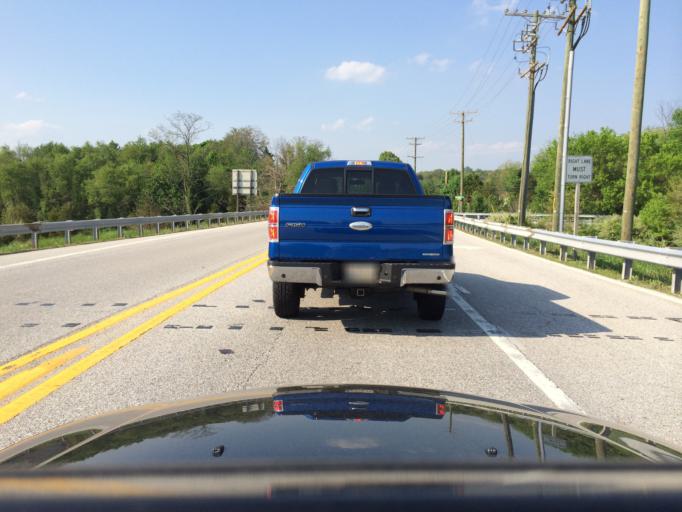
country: US
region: Maryland
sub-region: Carroll County
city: Sykesville
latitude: 39.3307
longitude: -77.0149
